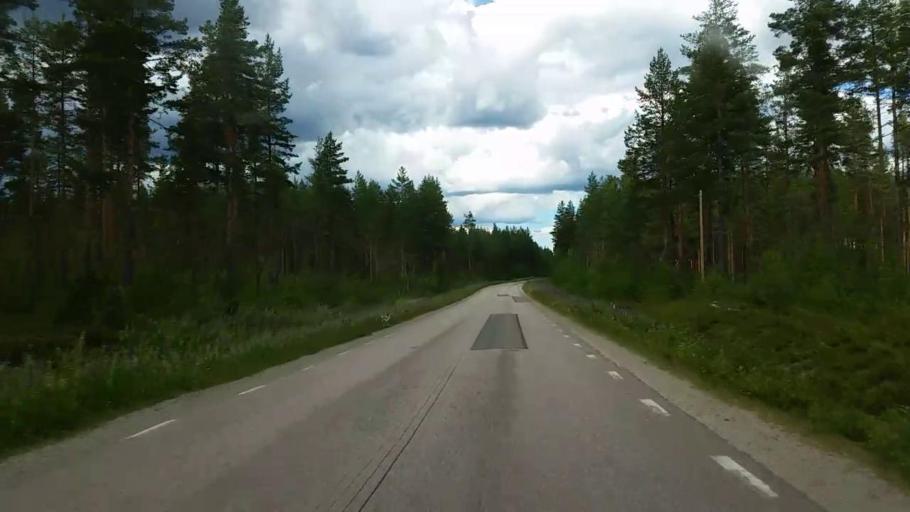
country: SE
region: Gaevleborg
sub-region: Ovanakers Kommun
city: Edsbyn
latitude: 61.4077
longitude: 15.8968
